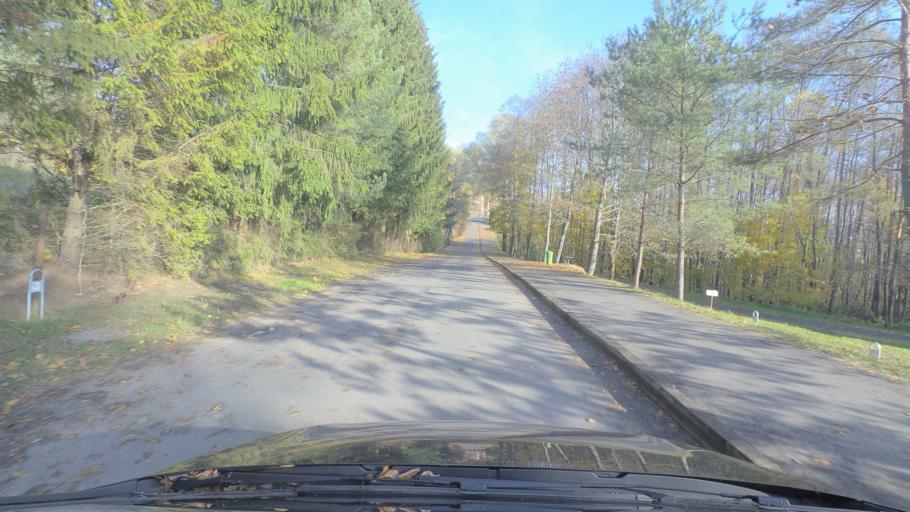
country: LT
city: Ignalina
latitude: 55.3375
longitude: 26.1483
